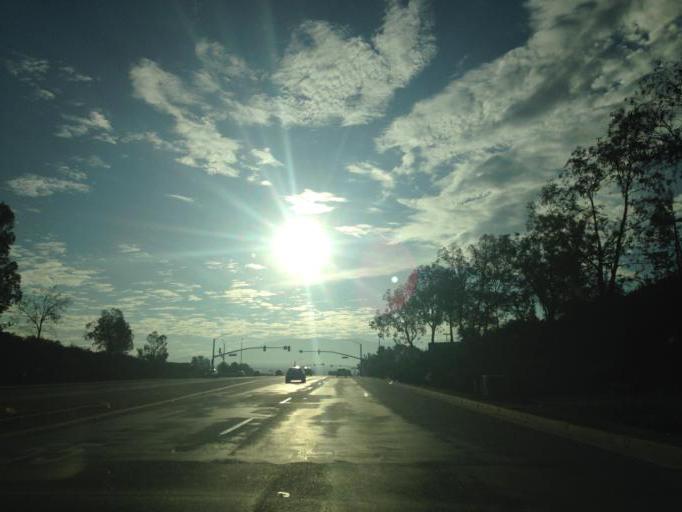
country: US
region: California
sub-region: Riverside County
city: Temecula
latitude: 33.4800
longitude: -117.1396
